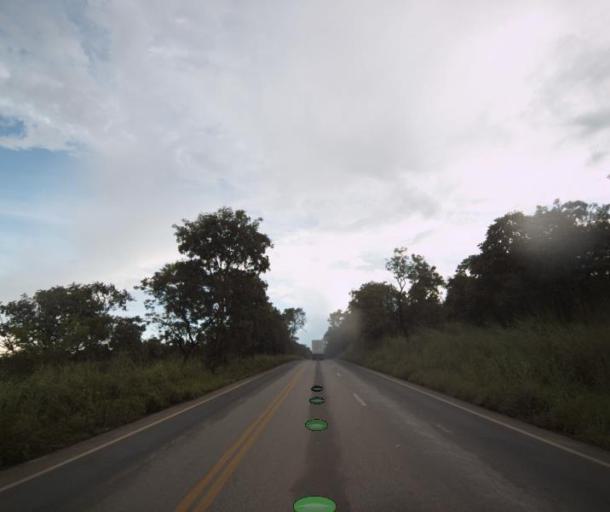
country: BR
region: Goias
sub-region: Porangatu
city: Porangatu
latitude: -13.9625
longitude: -49.0892
